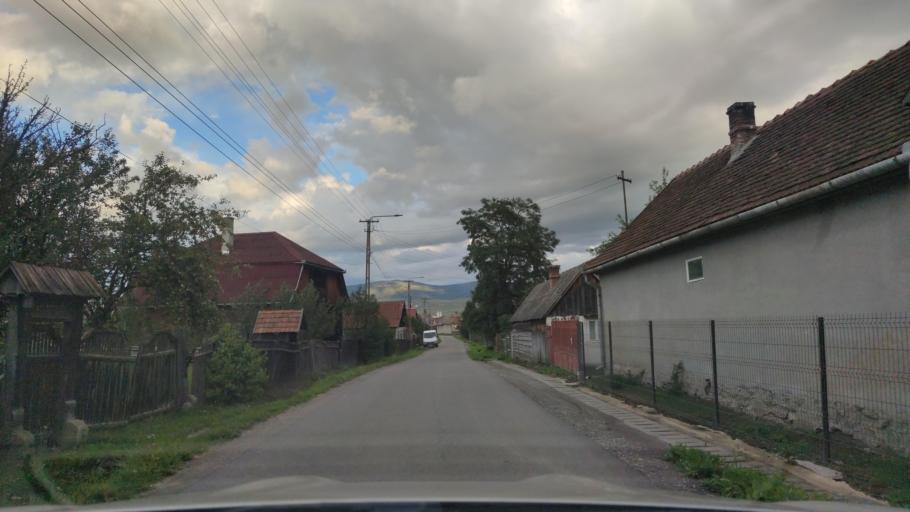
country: RO
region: Harghita
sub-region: Comuna Remetea
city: Remetea
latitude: 46.8045
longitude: 25.4525
